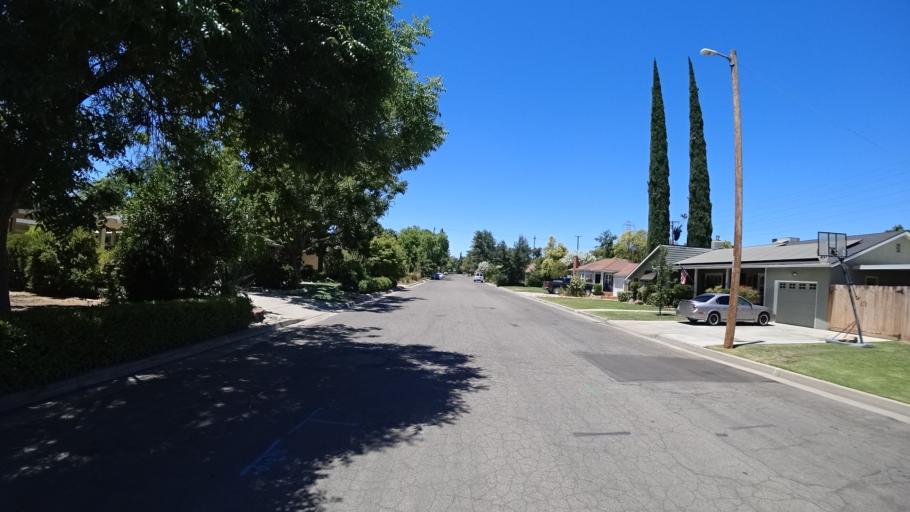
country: US
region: California
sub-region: Fresno County
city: Fresno
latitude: 36.7863
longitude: -119.8011
